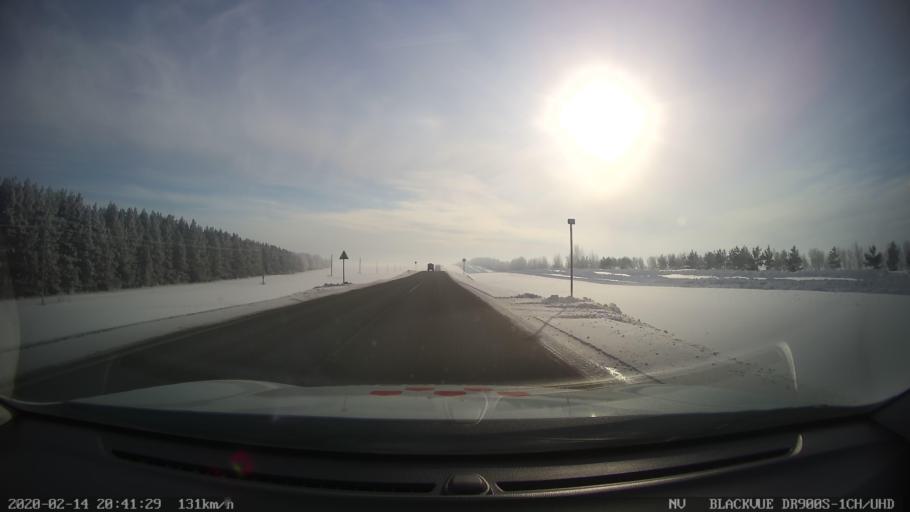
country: RU
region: Tatarstan
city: Kuybyshevskiy Zaton
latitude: 55.3301
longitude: 49.1215
